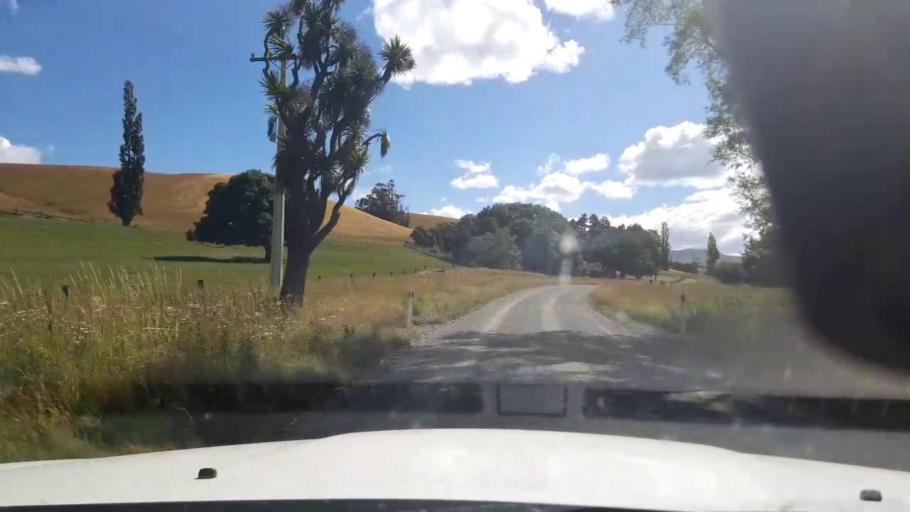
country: NZ
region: Canterbury
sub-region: Timaru District
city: Pleasant Point
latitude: -44.3179
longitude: 170.9425
